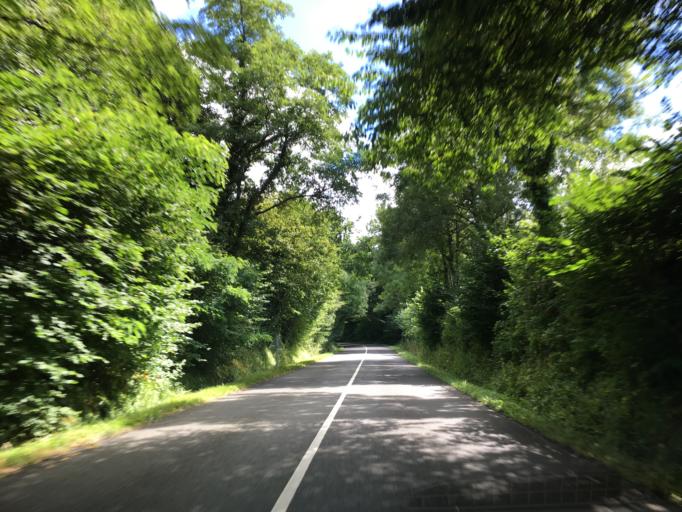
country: FR
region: Lower Normandy
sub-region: Departement du Calvados
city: Houlgate
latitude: 49.2821
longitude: -0.0806
